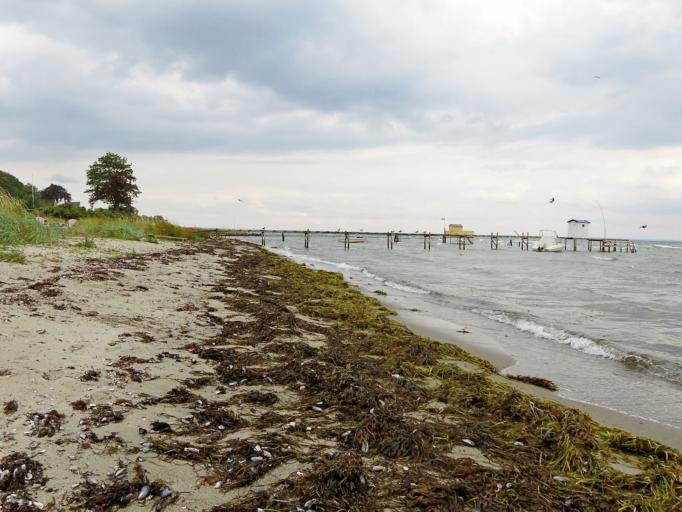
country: DK
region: Capital Region
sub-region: Fredensborg Kommune
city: Humlebaek
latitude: 55.9450
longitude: 12.5288
